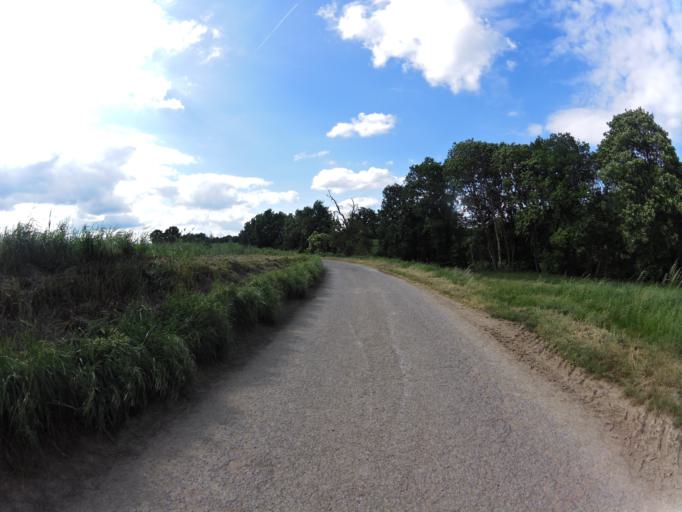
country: DE
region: Bavaria
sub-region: Regierungsbezirk Unterfranken
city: Gaukonigshofen
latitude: 49.6563
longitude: 10.0242
